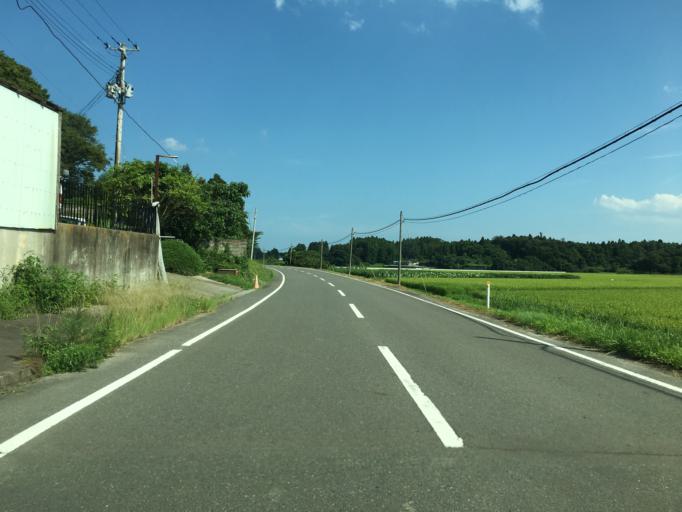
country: JP
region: Miyagi
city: Marumori
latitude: 37.7893
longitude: 140.9353
